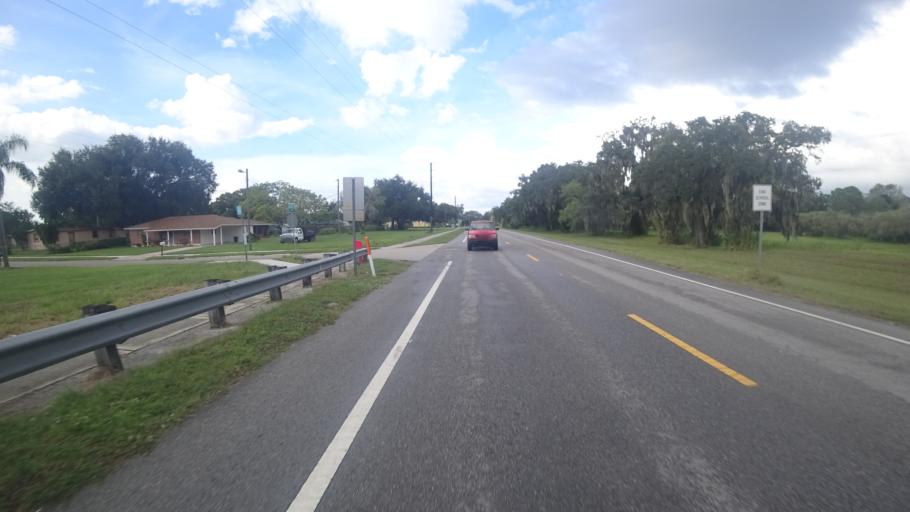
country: US
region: Florida
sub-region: Manatee County
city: Memphis
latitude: 27.5366
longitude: -82.5484
